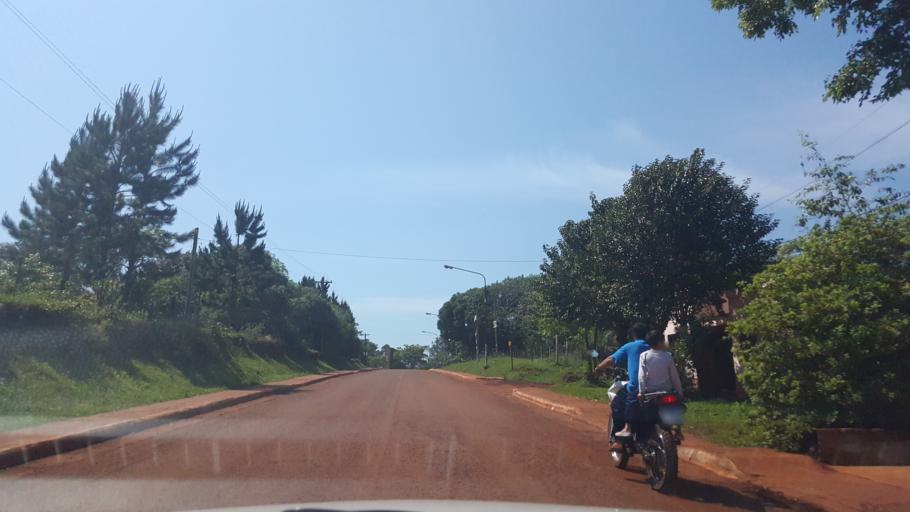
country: AR
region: Corrientes
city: San Carlos
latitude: -27.7465
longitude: -55.8909
